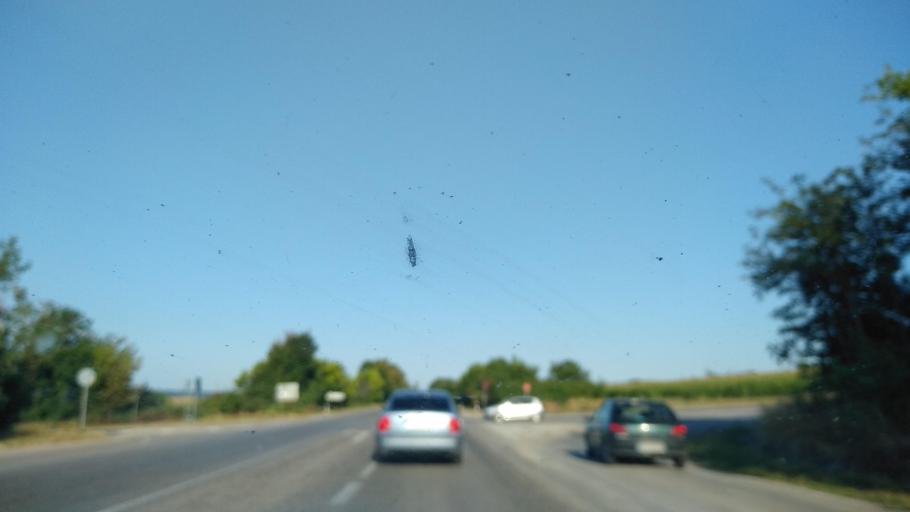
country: BG
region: Gabrovo
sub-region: Obshtina Dryanovo
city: Dryanovo
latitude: 43.0881
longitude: 25.4637
